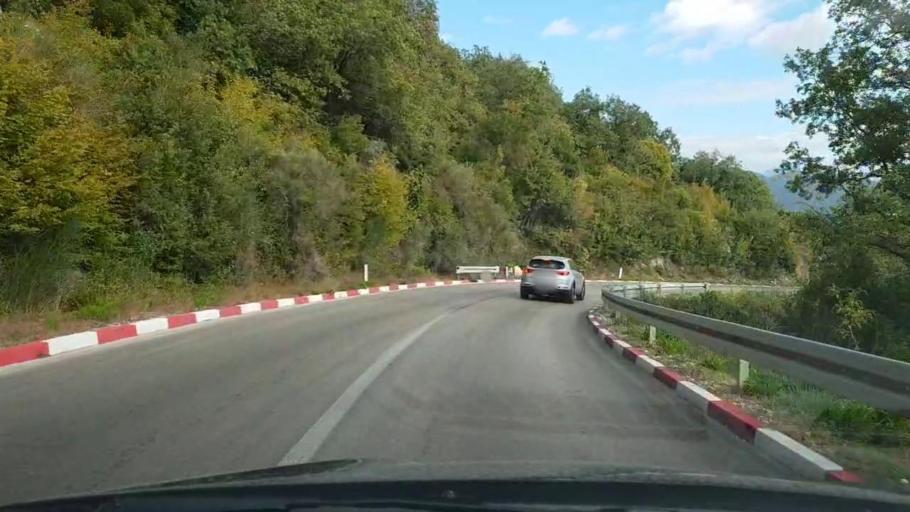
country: ME
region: Herceg Novi
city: Herceg-Novi
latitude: 42.4669
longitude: 18.5398
